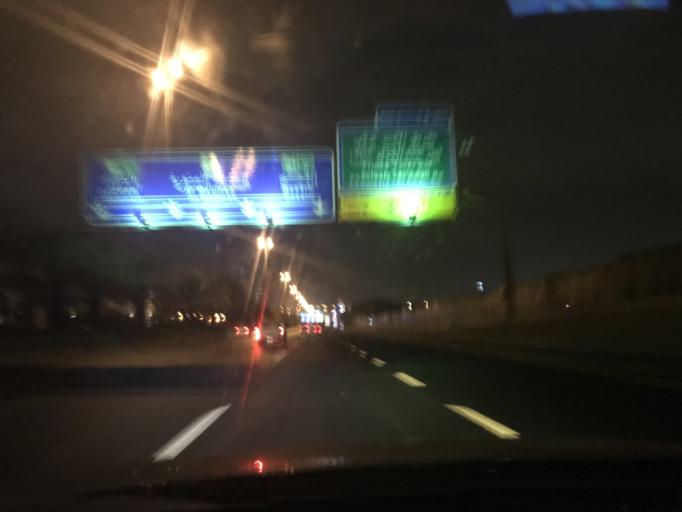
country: SA
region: Ar Riyad
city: Riyadh
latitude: 24.7443
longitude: 46.6081
